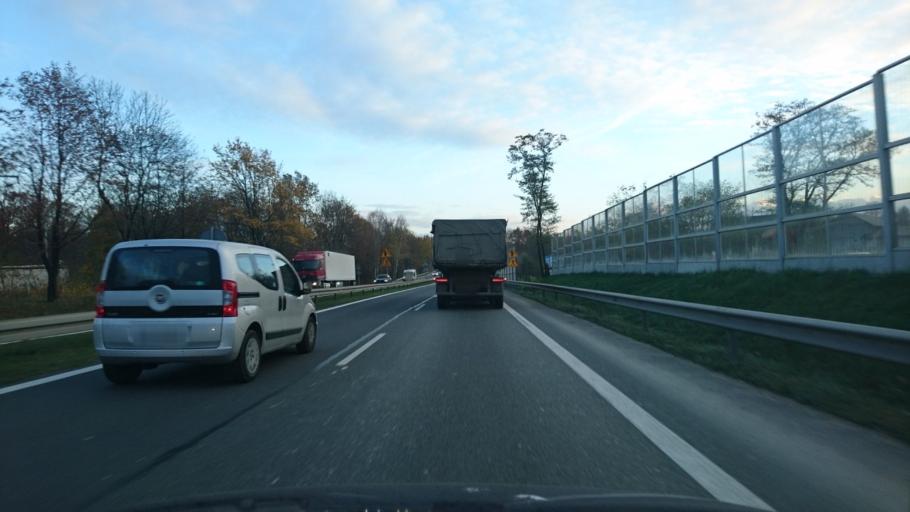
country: PL
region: Silesian Voivodeship
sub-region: Powiat bielski
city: Czechowice-Dziedzice
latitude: 49.8905
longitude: 18.9946
